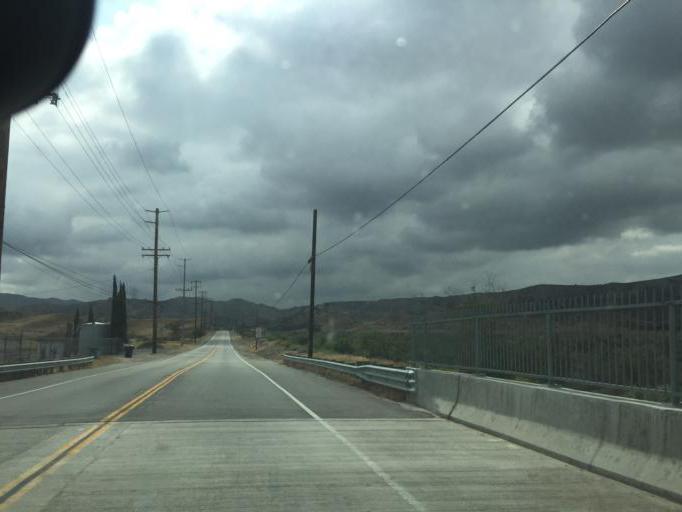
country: US
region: California
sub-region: Los Angeles County
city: Santa Clarita
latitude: 34.4738
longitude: -118.4671
